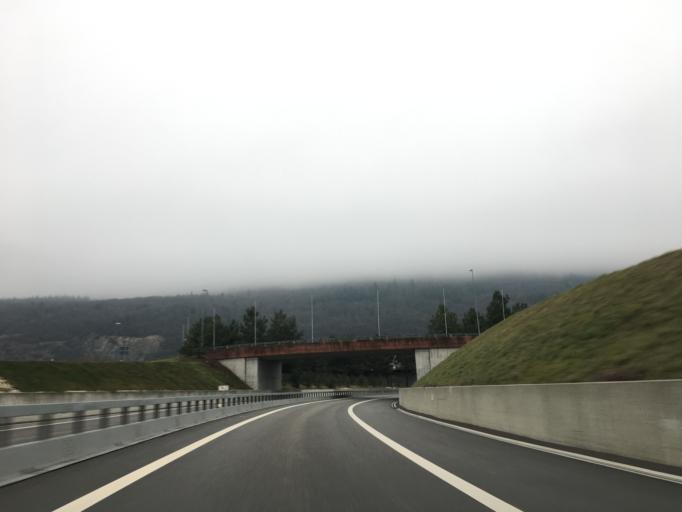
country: CH
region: Bern
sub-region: Biel/Bienne District
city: Orpund
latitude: 47.1560
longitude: 7.2853
